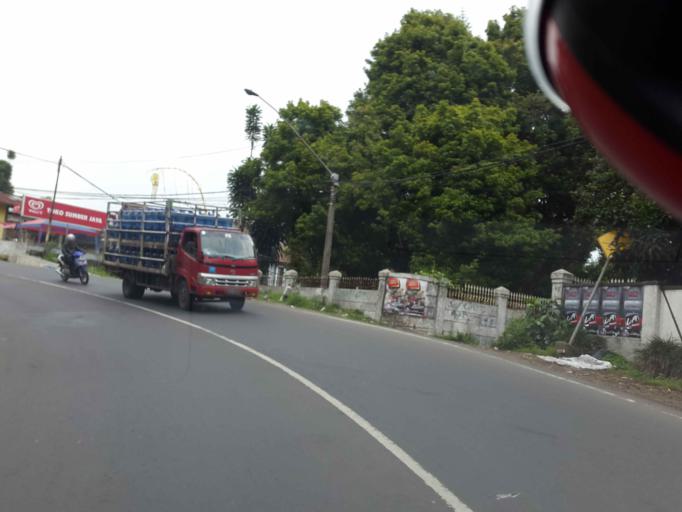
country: ID
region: West Java
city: Lembang
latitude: -6.8384
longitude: 107.5989
